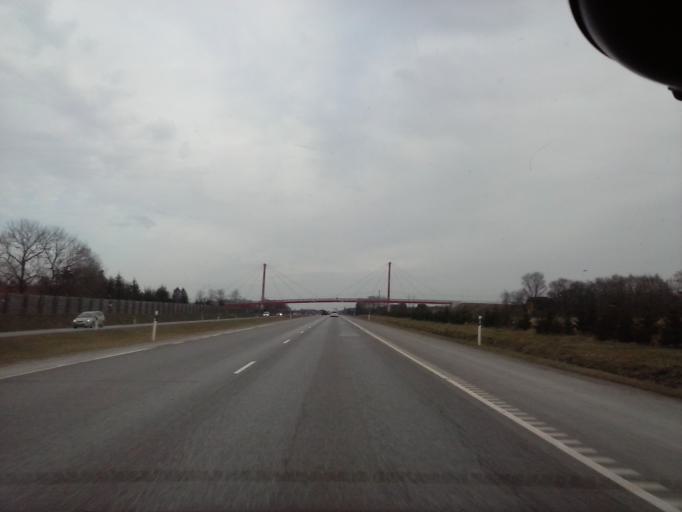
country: EE
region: Harju
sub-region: Rae vald
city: Vaida
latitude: 59.2829
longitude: 24.9754
